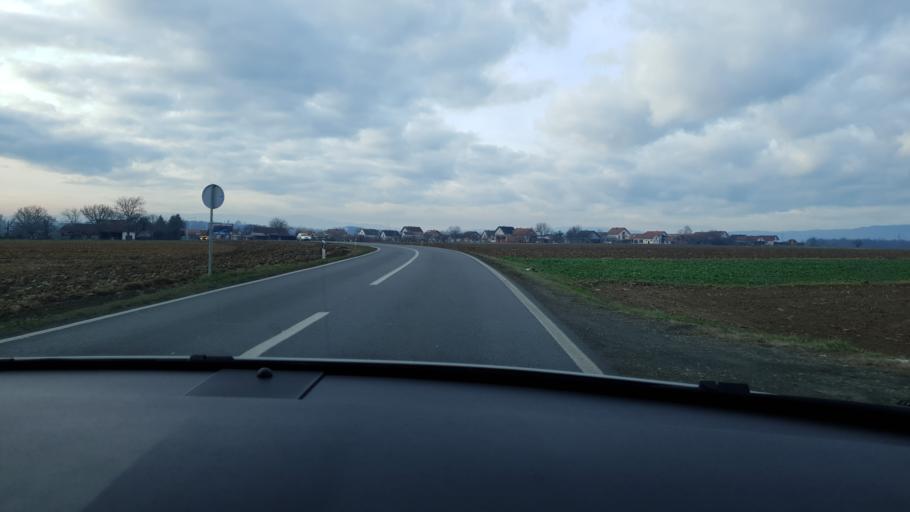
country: HR
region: Pozesko-Slavonska
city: Jaksic
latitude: 45.3573
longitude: 17.7436
